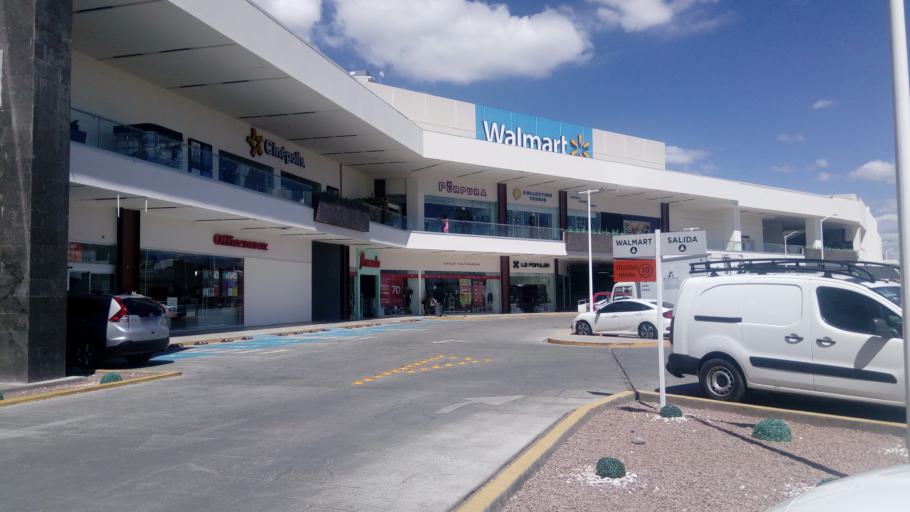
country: MX
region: Durango
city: Victoria de Durango
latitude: 24.0127
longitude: -104.6914
